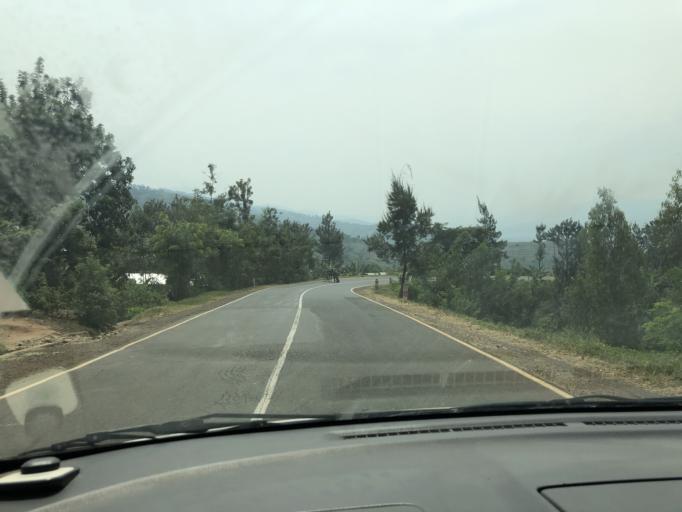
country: RW
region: Western Province
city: Cyangugu
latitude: -2.6706
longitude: 28.9946
